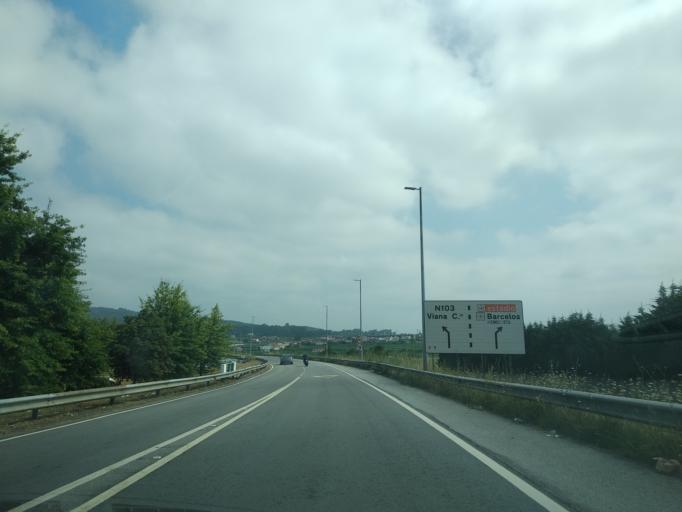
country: PT
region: Braga
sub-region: Barcelos
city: Vila Frescainha
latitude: 41.5327
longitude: -8.6385
